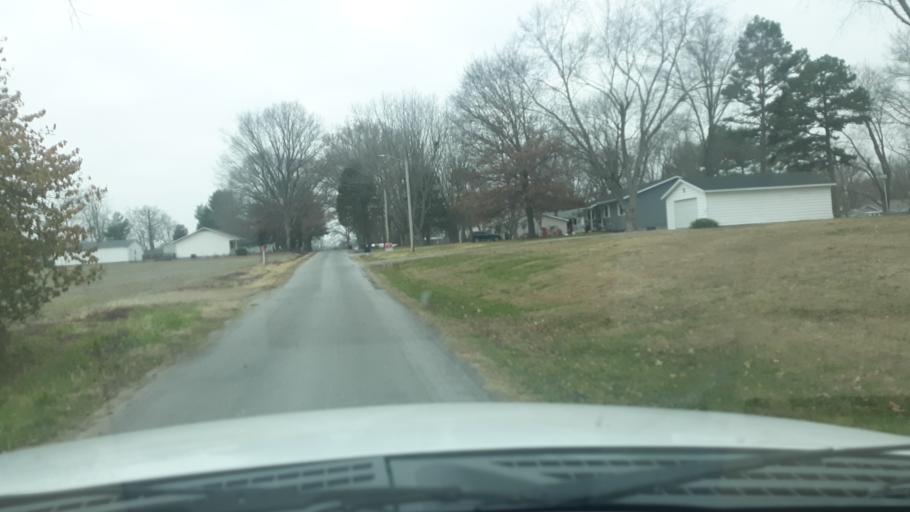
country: US
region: Illinois
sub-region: Saline County
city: Harrisburg
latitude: 37.8377
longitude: -88.6063
